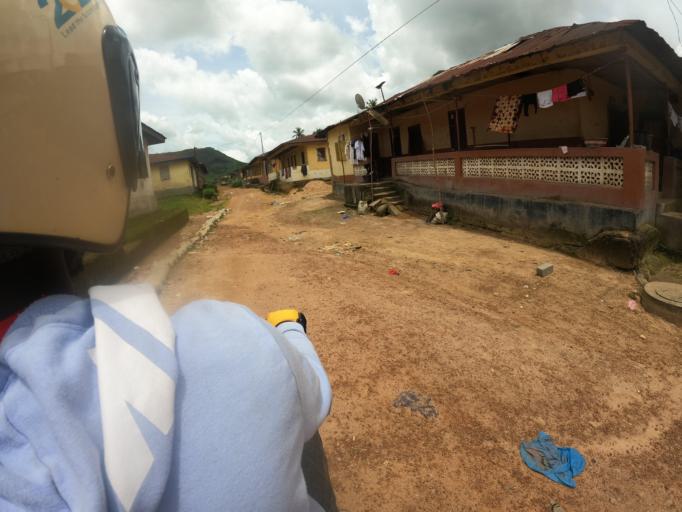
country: SL
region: Northern Province
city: Makeni
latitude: 8.8908
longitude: -12.0506
